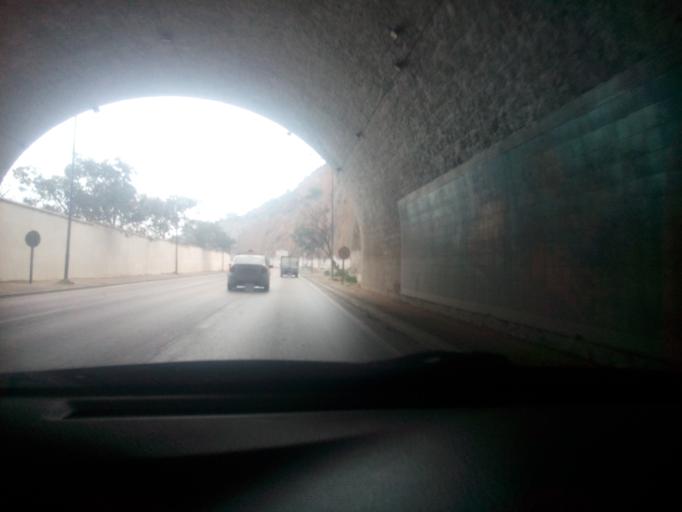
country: DZ
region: Oran
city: Mers el Kebir
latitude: 35.7123
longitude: -0.6736
